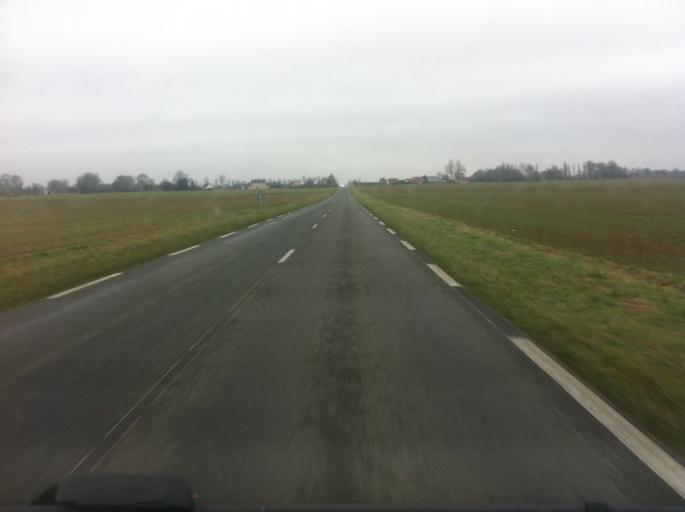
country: FR
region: Haute-Normandie
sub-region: Departement de l'Eure
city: Manneville-sur-Risle
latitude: 49.3730
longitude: 0.5409
